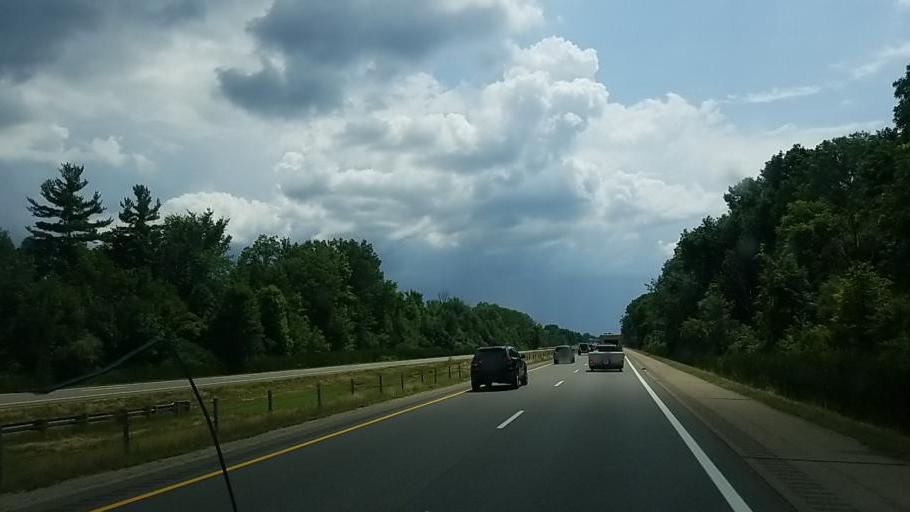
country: US
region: Michigan
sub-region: Kent County
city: Northview
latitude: 42.9979
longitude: -85.6050
